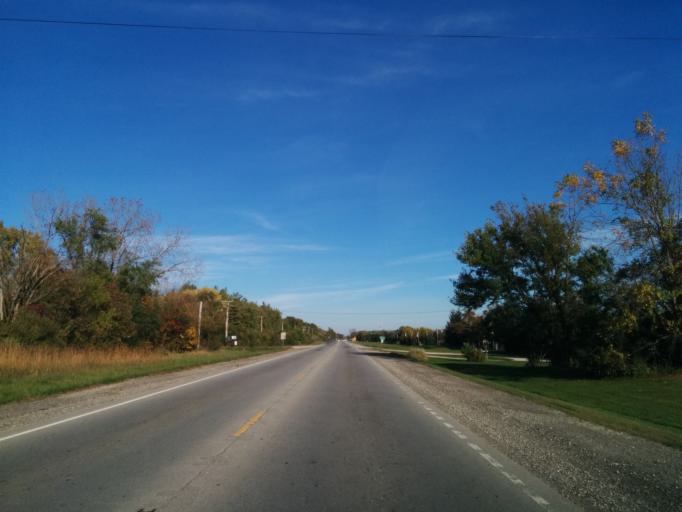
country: US
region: Illinois
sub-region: Kane County
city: Batavia
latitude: 41.8153
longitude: -88.2643
